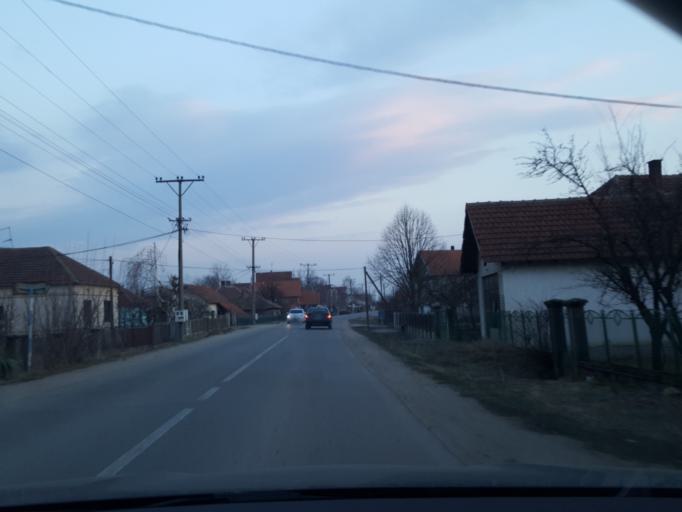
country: RS
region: Central Serbia
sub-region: Nisavski Okrug
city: Aleksinac
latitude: 43.5002
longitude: 21.7038
